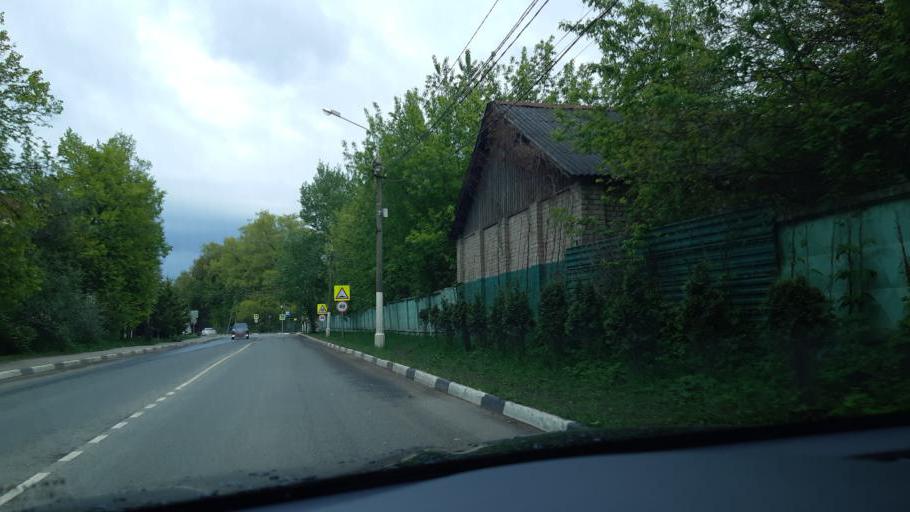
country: RU
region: Moskovskaya
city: Dolgoprudnyy
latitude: 55.9517
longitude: 37.4990
